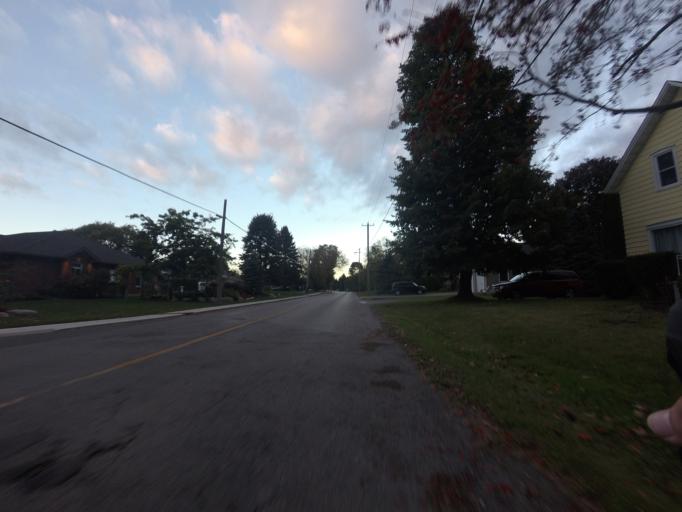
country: CA
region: Ontario
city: Quinte West
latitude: 44.0255
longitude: -77.7265
